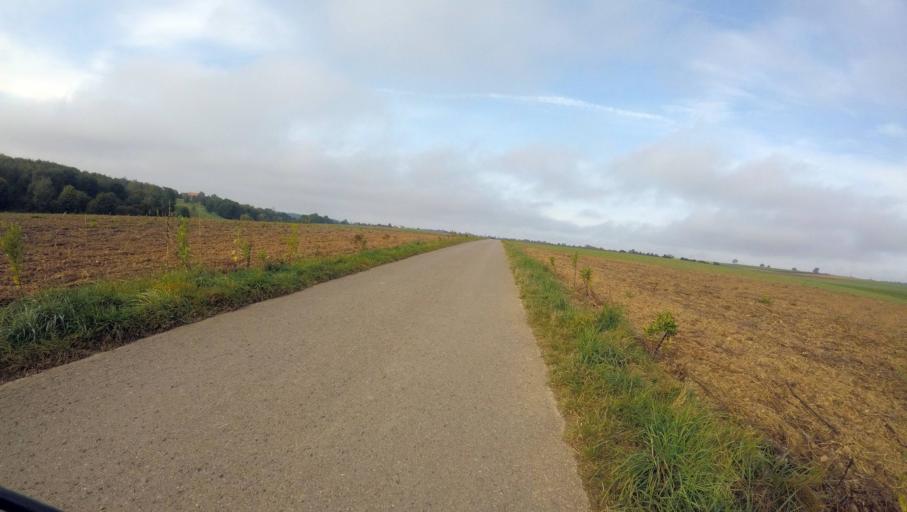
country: DE
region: Baden-Wuerttemberg
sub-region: Regierungsbezirk Stuttgart
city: Motzingen
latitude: 48.5339
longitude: 8.8031
